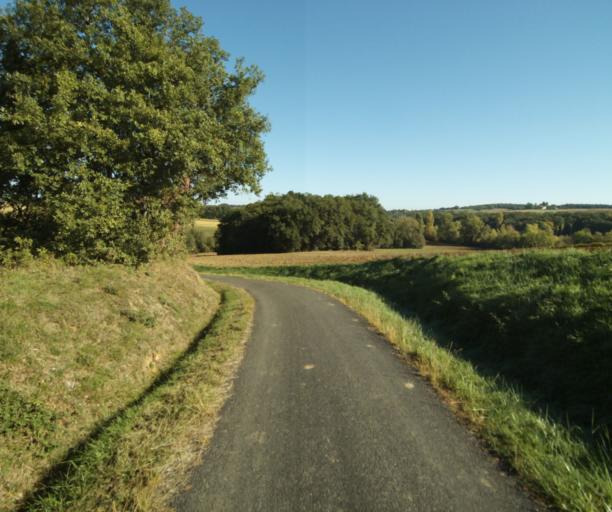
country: FR
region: Midi-Pyrenees
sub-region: Departement du Gers
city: Gondrin
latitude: 43.8264
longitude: 0.2421
